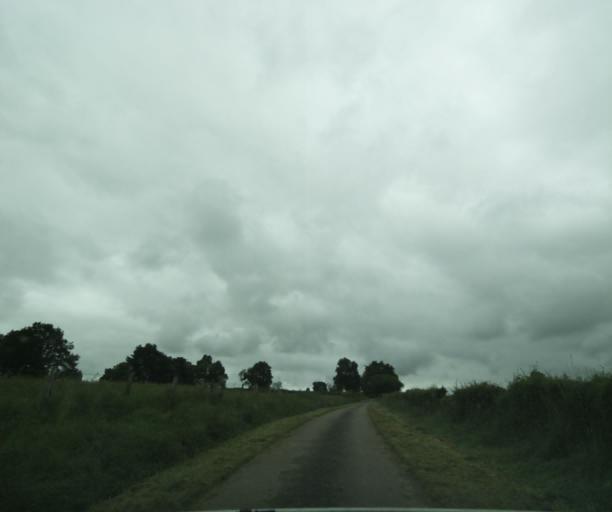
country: FR
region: Bourgogne
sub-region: Departement de Saone-et-Loire
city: Charolles
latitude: 46.4675
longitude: 4.2983
